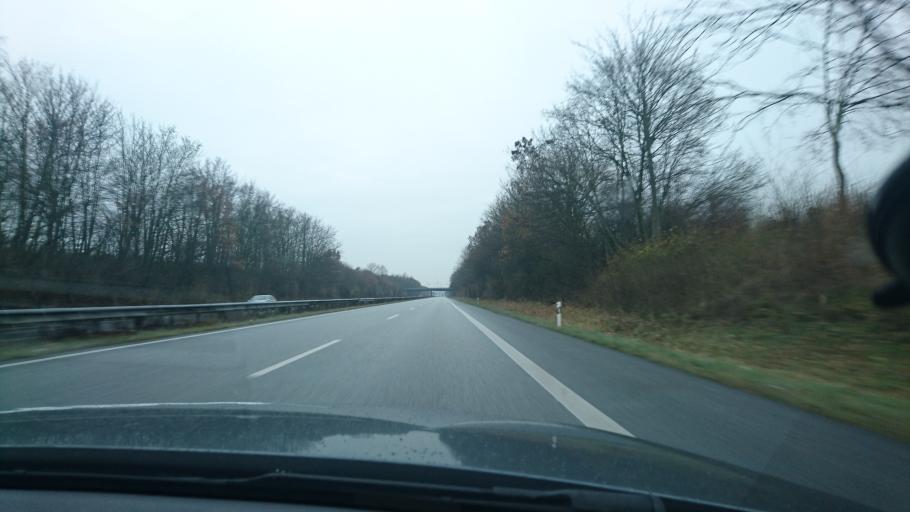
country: DE
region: Schleswig-Holstein
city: Manhagen
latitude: 54.1929
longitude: 10.8967
